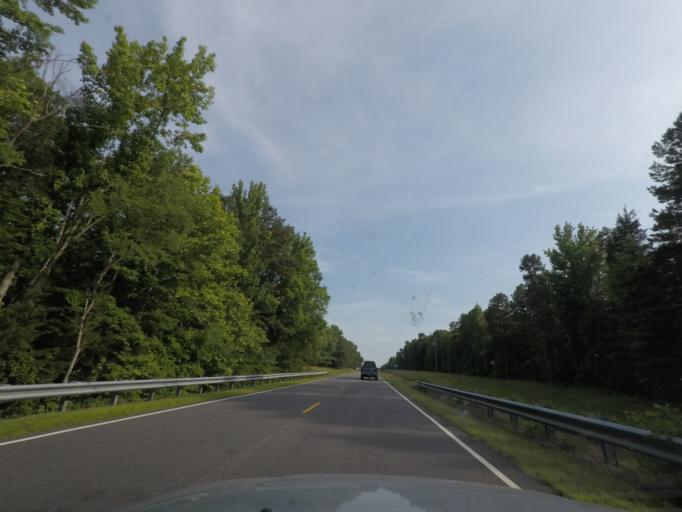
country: US
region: Virginia
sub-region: Mecklenburg County
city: Clarksville
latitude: 36.7131
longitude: -78.6311
